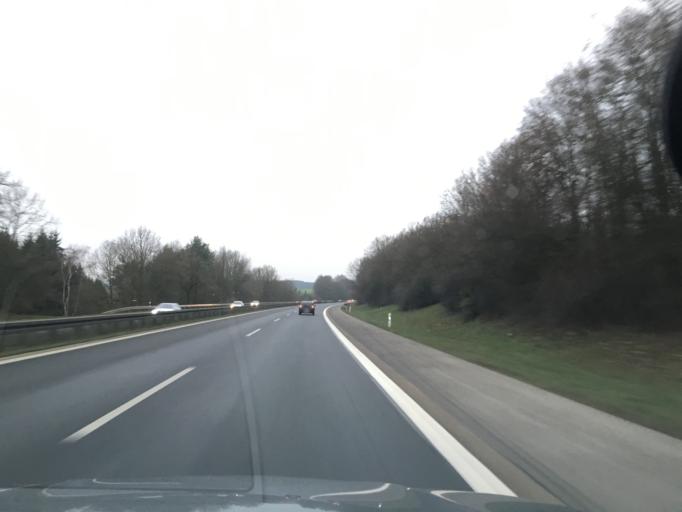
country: DE
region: Bavaria
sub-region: Regierungsbezirk Mittelfranken
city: Vestenbergsgreuth
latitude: 49.7330
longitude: 10.6661
